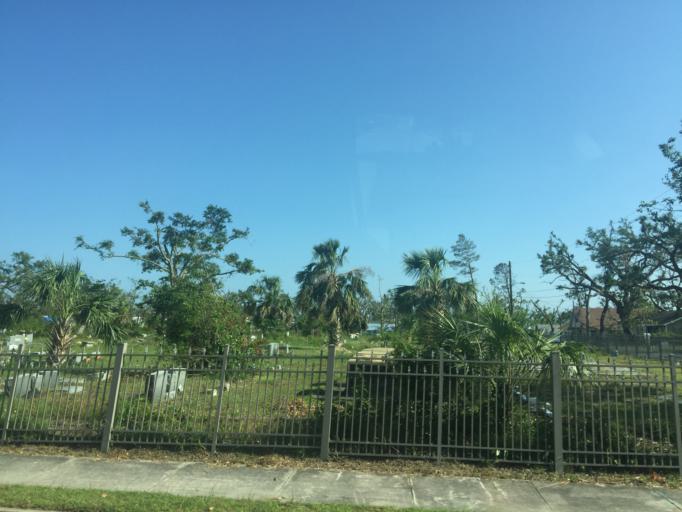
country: US
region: Florida
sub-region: Bay County
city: Springfield
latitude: 30.1532
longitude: -85.6270
